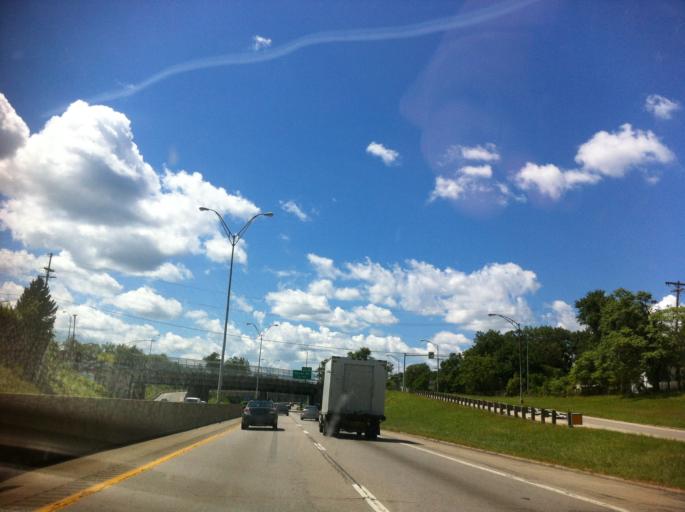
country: US
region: Ohio
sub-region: Lucas County
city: Ottawa Hills
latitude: 41.6856
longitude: -83.6120
